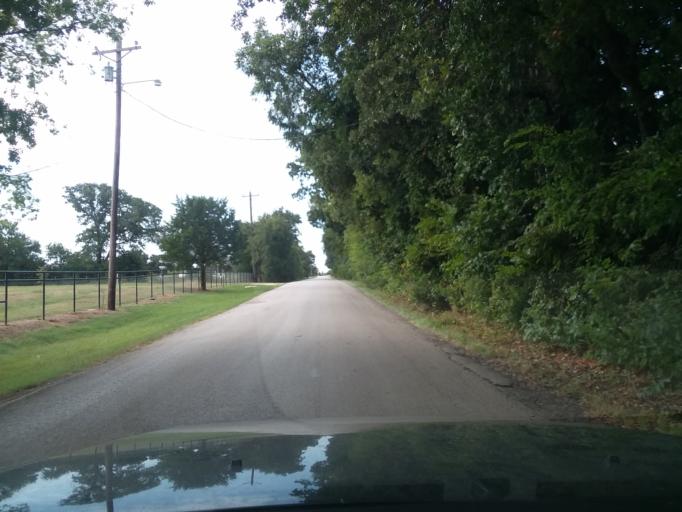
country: US
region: Texas
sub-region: Denton County
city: Bartonville
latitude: 33.1062
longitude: -97.1312
